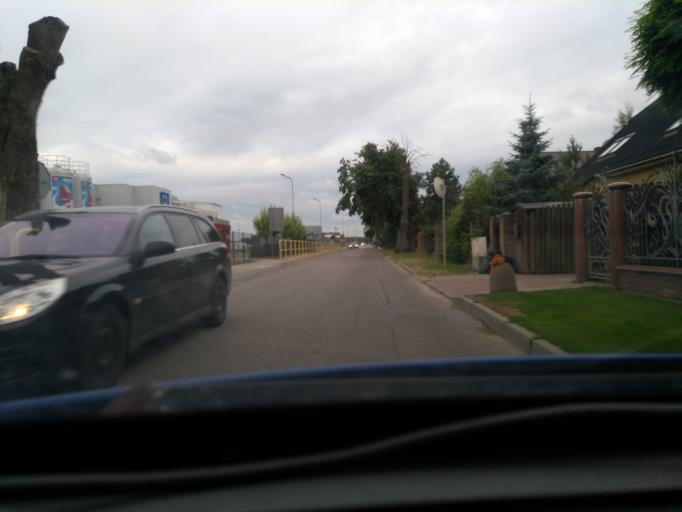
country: PL
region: Pomeranian Voivodeship
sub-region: Powiat kartuski
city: Banino
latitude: 54.3879
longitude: 18.4060
